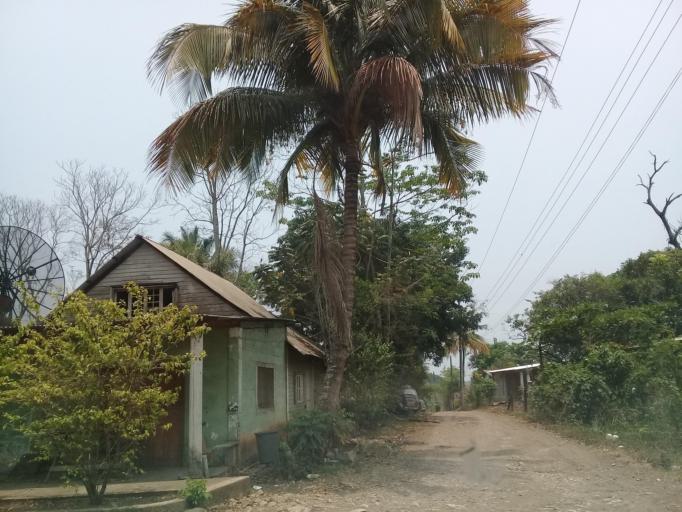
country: MX
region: Veracruz
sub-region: Tezonapa
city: Laguna Chica (Pueblo Nuevo)
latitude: 18.5419
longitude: -96.7367
